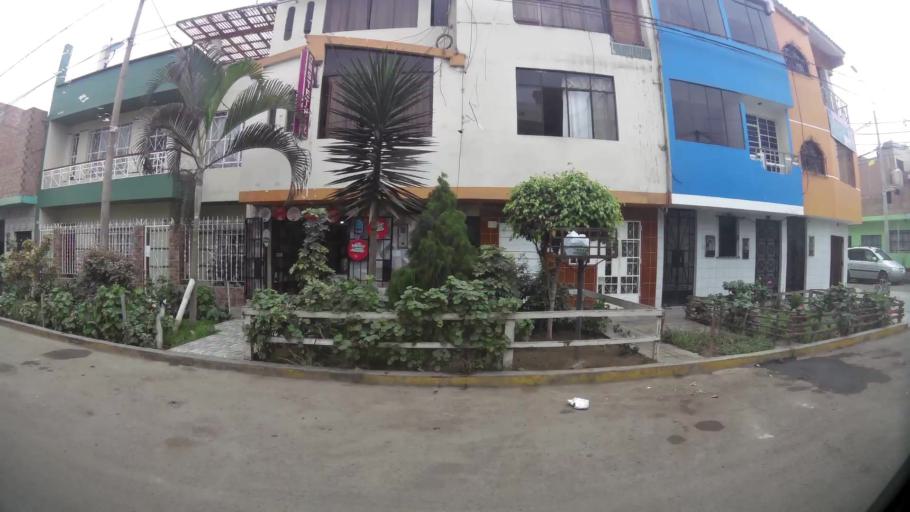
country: PE
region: Lima
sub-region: Provincia de Huaral
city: Huaral
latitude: -11.4987
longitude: -77.2099
